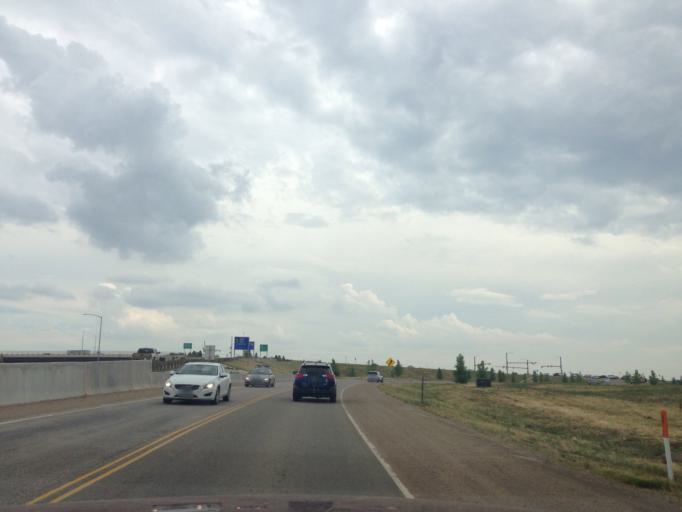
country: US
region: Colorado
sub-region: Weld County
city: Windsor
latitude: 40.4827
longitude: -104.9924
